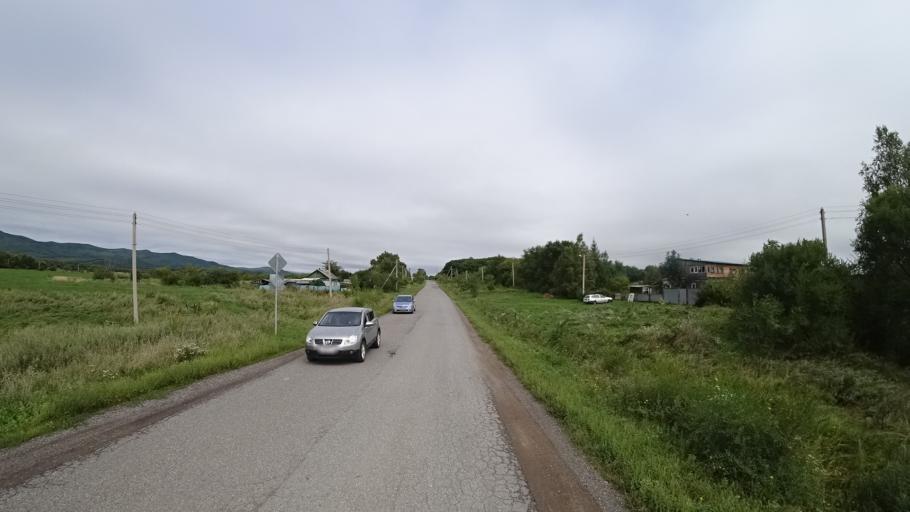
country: RU
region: Primorskiy
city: Lyalichi
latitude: 44.0732
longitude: 132.4648
